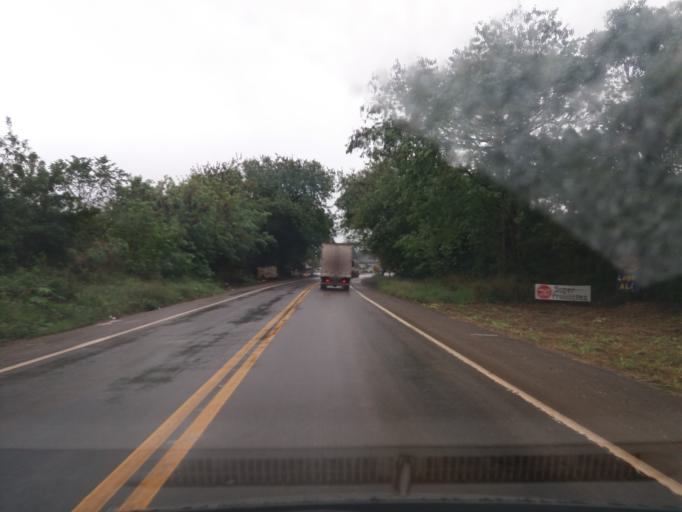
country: BR
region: Parana
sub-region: Realeza
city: Realeza
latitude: -25.4936
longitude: -53.5988
